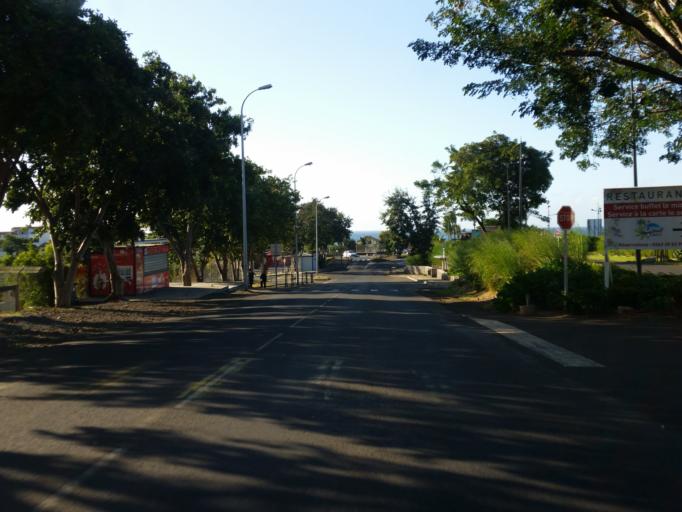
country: RE
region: Reunion
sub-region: Reunion
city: Saint-Denis
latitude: -20.8890
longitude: 55.4720
